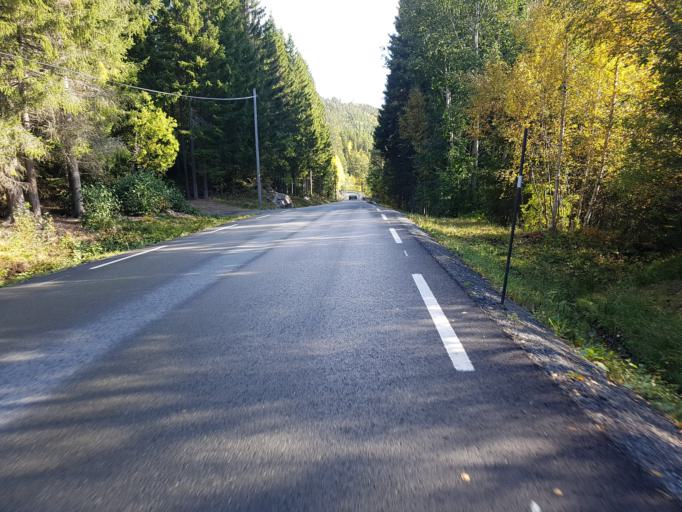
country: NO
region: Sor-Trondelag
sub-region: Malvik
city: Malvik
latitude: 63.3766
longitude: 10.6054
